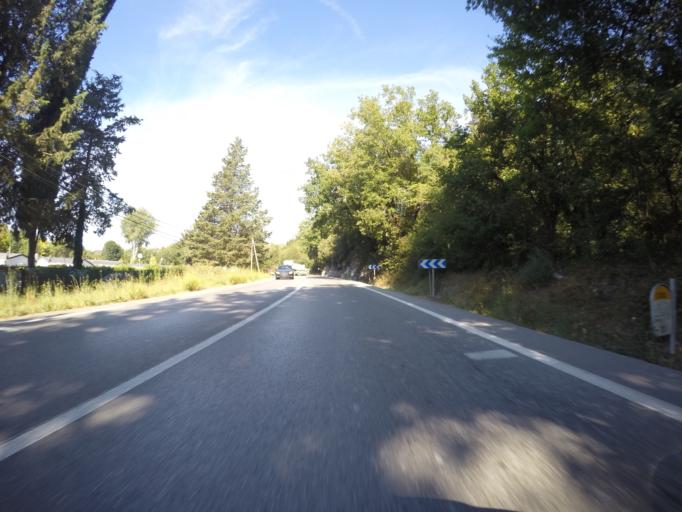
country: FR
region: Provence-Alpes-Cote d'Azur
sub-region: Departement des Alpes-Maritimes
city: Villeneuve-Loubet
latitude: 43.6606
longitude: 7.1017
